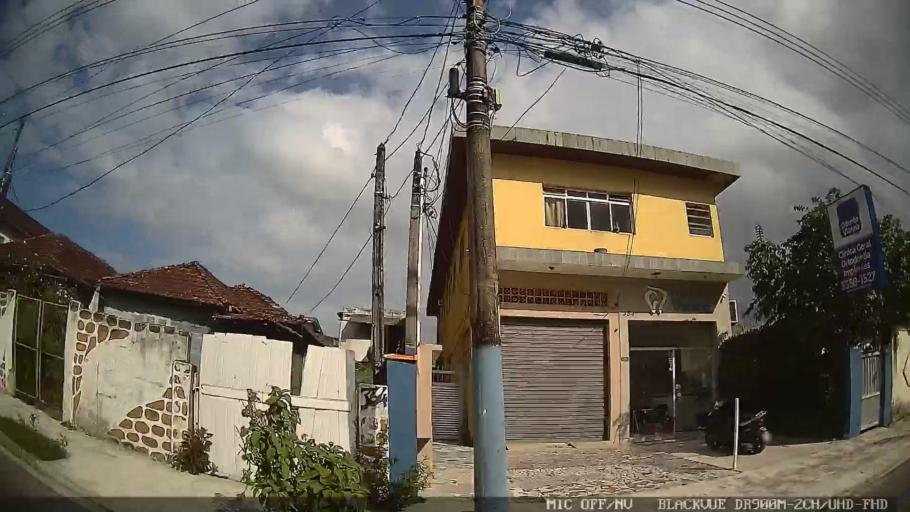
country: BR
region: Sao Paulo
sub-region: Guaruja
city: Guaruja
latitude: -23.9941
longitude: -46.2861
